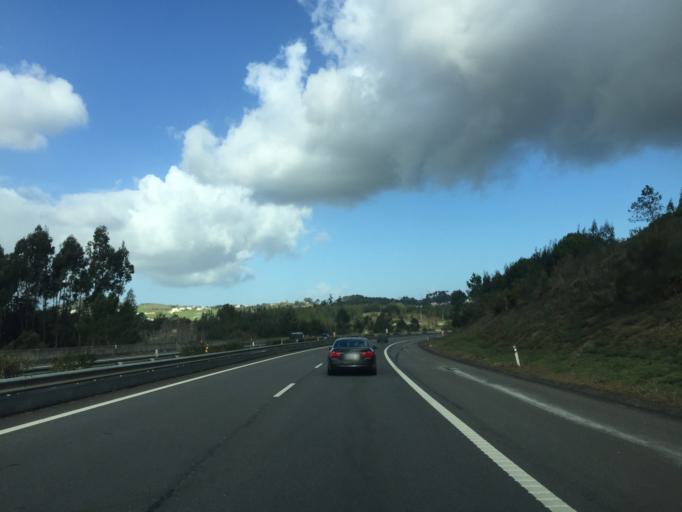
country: PT
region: Lisbon
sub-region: Mafra
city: Venda do Pinheiro
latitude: 38.9323
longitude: -9.2187
